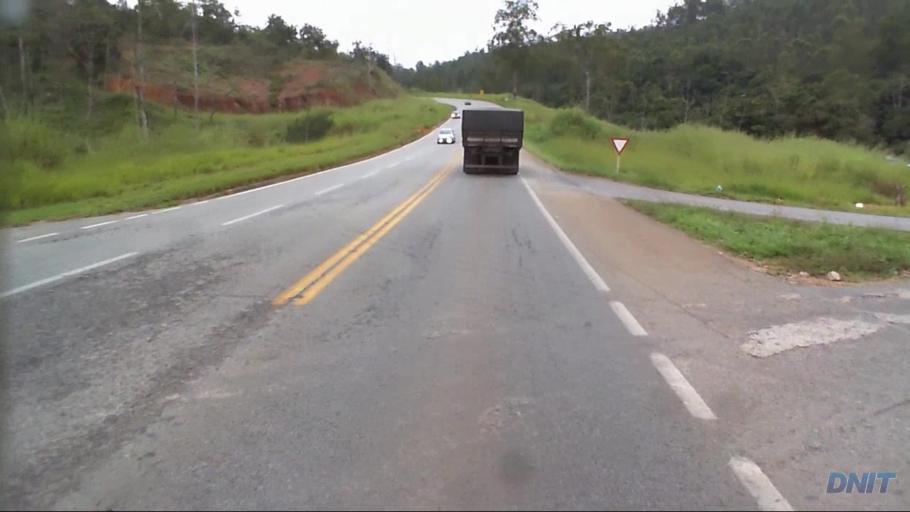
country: BR
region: Minas Gerais
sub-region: Nova Era
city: Nova Era
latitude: -19.8237
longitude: -43.0798
